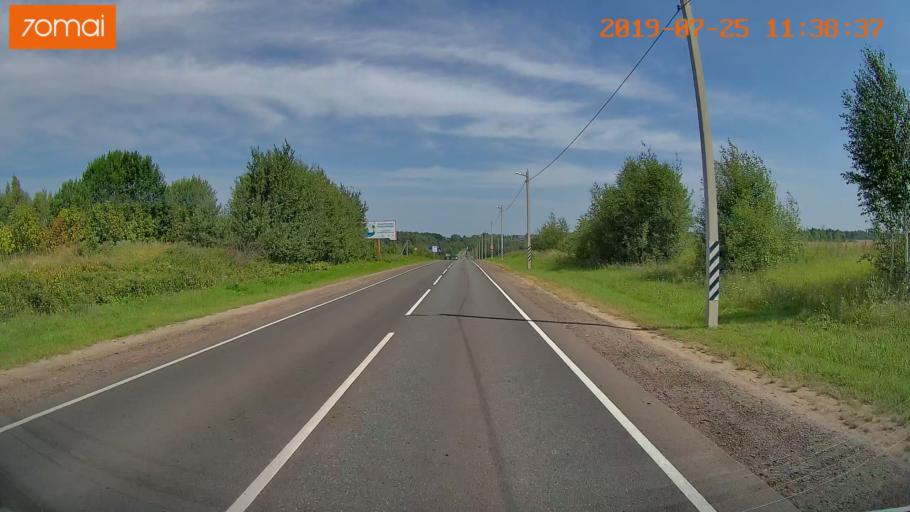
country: RU
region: Ivanovo
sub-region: Privolzhskiy Rayon
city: Ples
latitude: 57.4427
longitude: 41.4856
